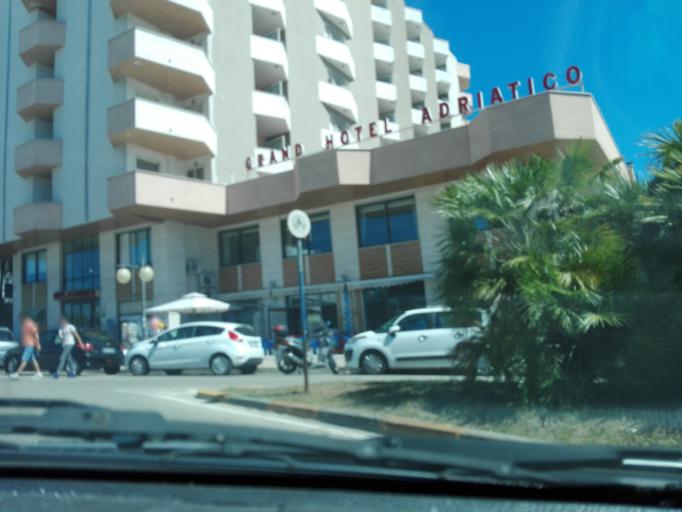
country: IT
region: Abruzzo
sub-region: Provincia di Pescara
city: Montesilvano Marina
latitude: 42.5222
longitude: 14.1546
